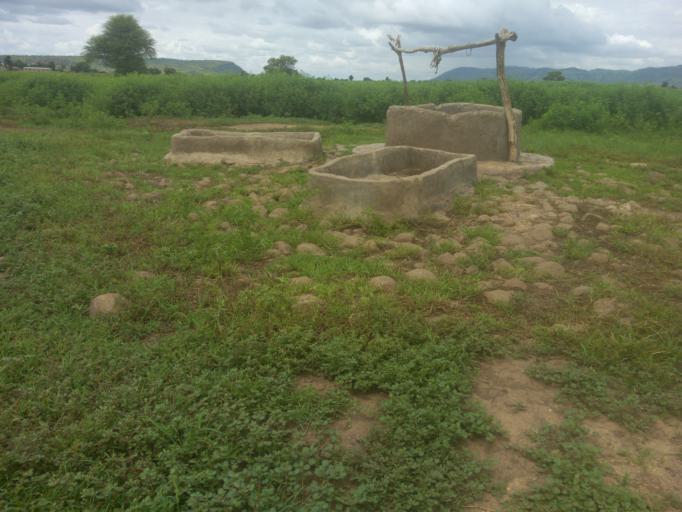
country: ML
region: Kayes
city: Yelimane
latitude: 14.6283
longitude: -10.7271
